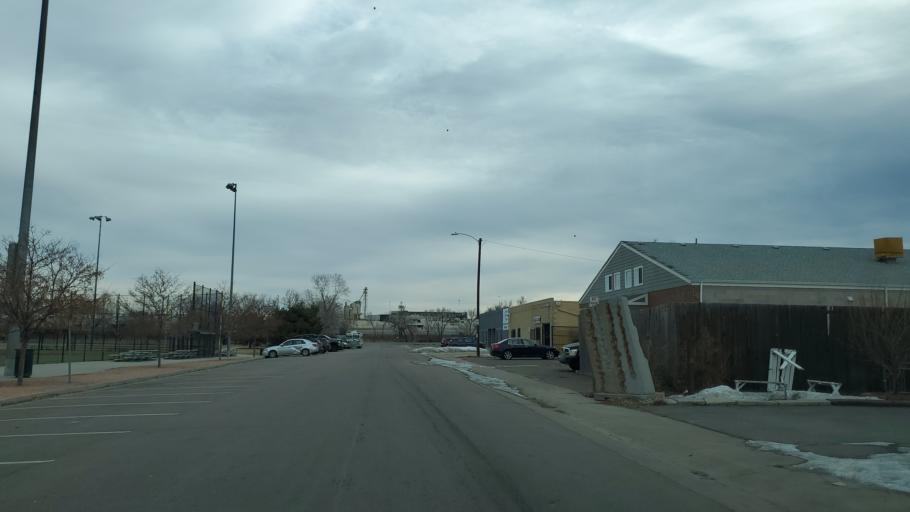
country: US
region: Colorado
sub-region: Denver County
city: Denver
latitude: 39.7130
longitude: -105.0035
